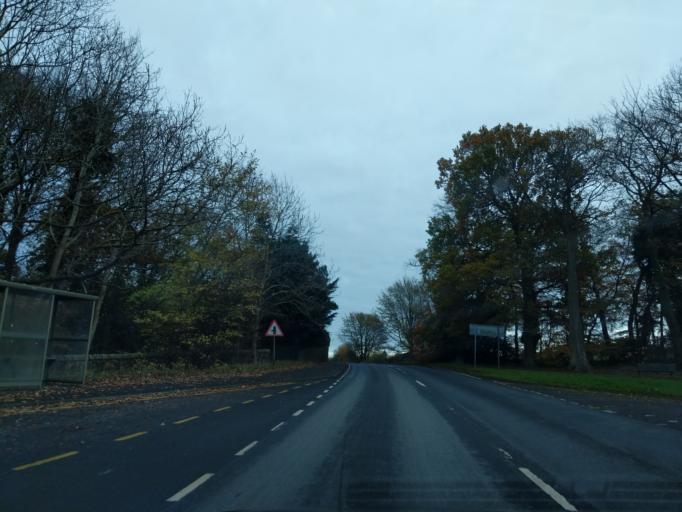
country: GB
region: Scotland
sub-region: West Lothian
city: Linlithgow
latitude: 56.0052
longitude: -3.5747
